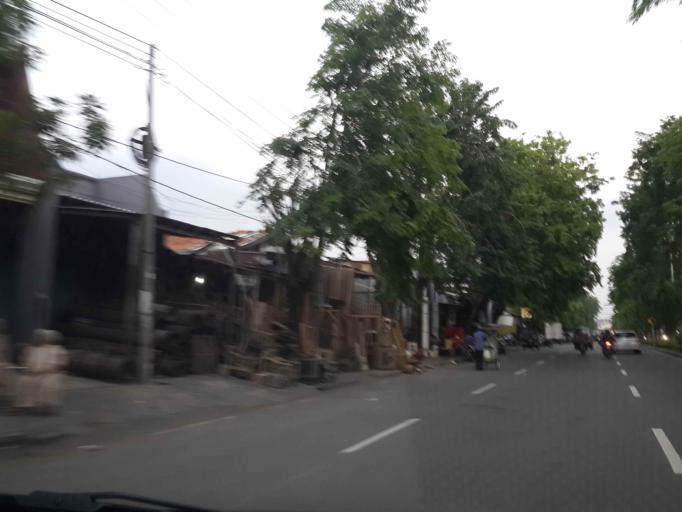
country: ID
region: East Java
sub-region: Kota Surabaya
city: Surabaya
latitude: -7.2519
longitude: 112.7206
